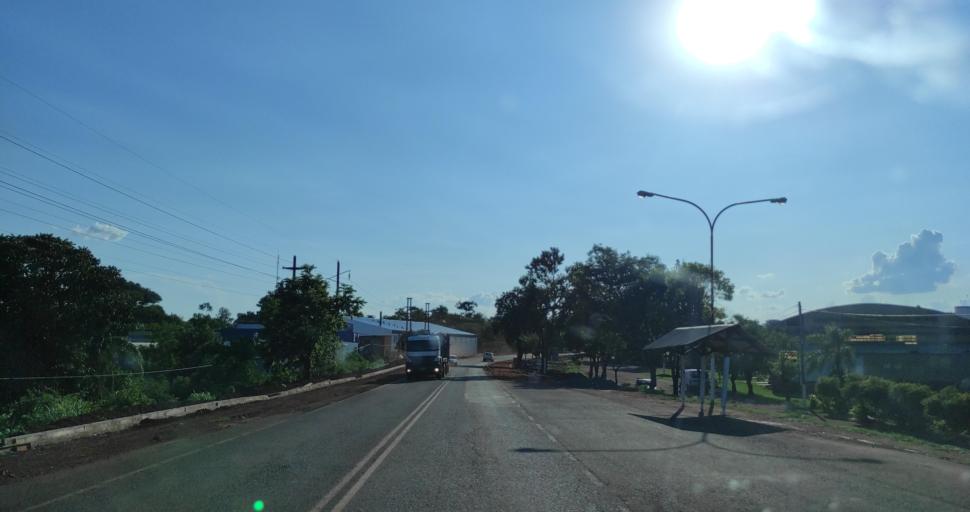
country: AR
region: Misiones
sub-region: Departamento de Eldorado
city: Eldorado
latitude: -26.4139
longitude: -54.4914
